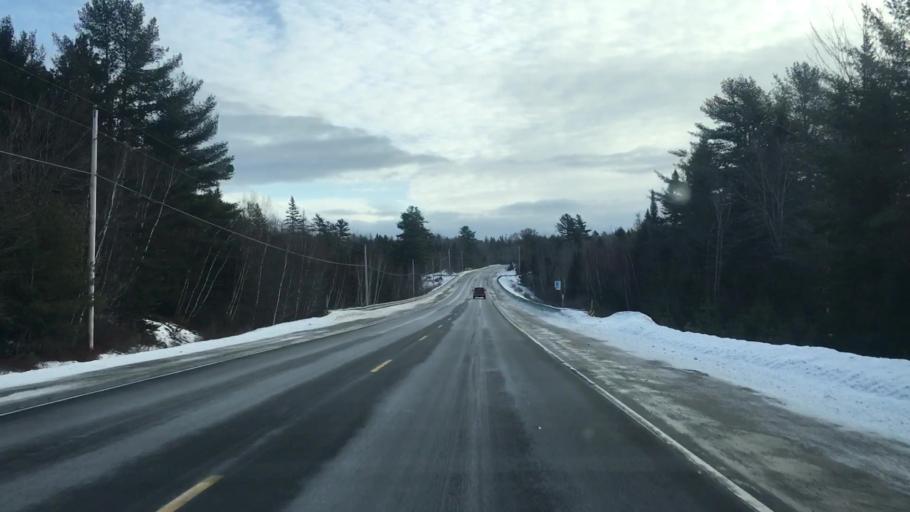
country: US
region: Maine
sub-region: Washington County
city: Machias
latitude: 44.9503
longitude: -67.6795
